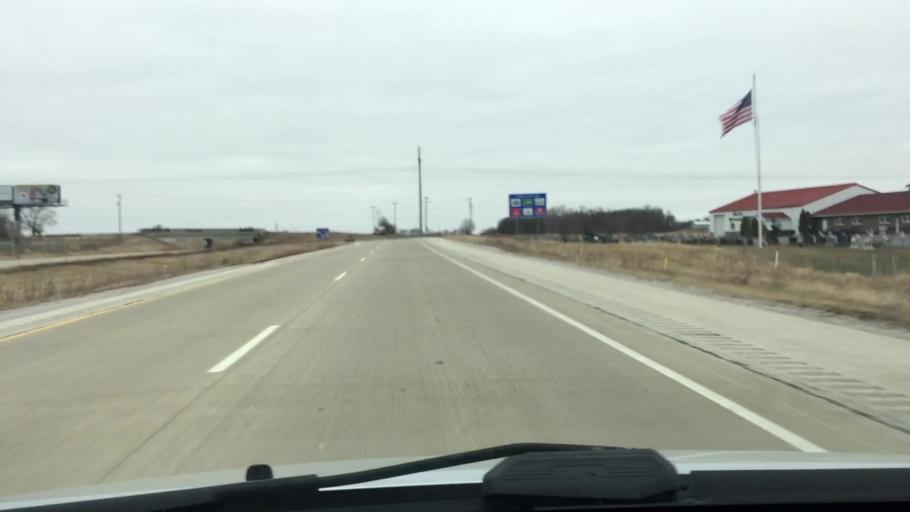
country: US
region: Wisconsin
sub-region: Jefferson County
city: Watertown
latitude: 43.1473
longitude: -88.7345
